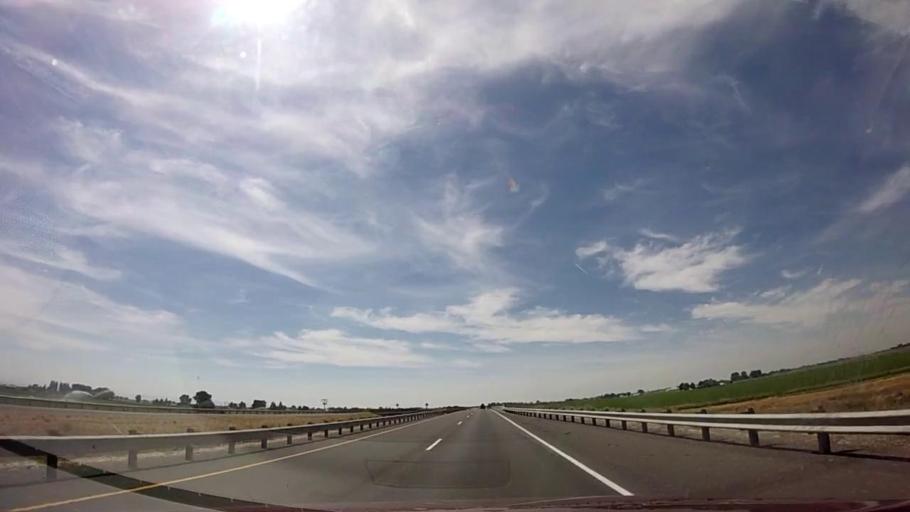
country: US
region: Idaho
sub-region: Minidoka County
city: Rupert
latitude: 42.5691
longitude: -113.6600
